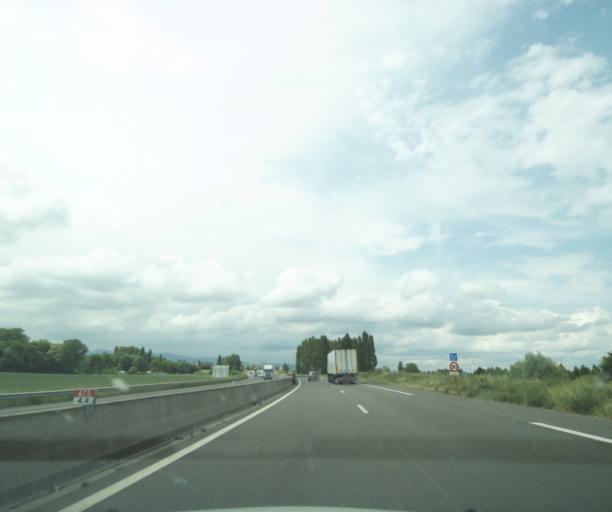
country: FR
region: Auvergne
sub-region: Departement du Puy-de-Dome
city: Perignat-les-Sarlieve
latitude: 45.7372
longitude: 3.1513
